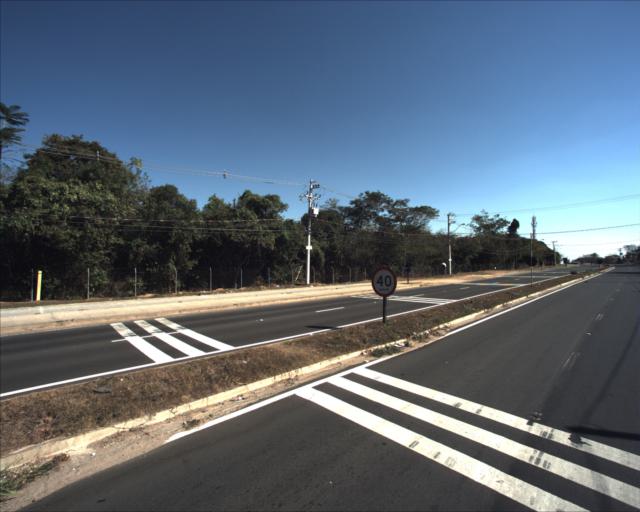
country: BR
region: Sao Paulo
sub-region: Sorocaba
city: Sorocaba
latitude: -23.3980
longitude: -47.3715
